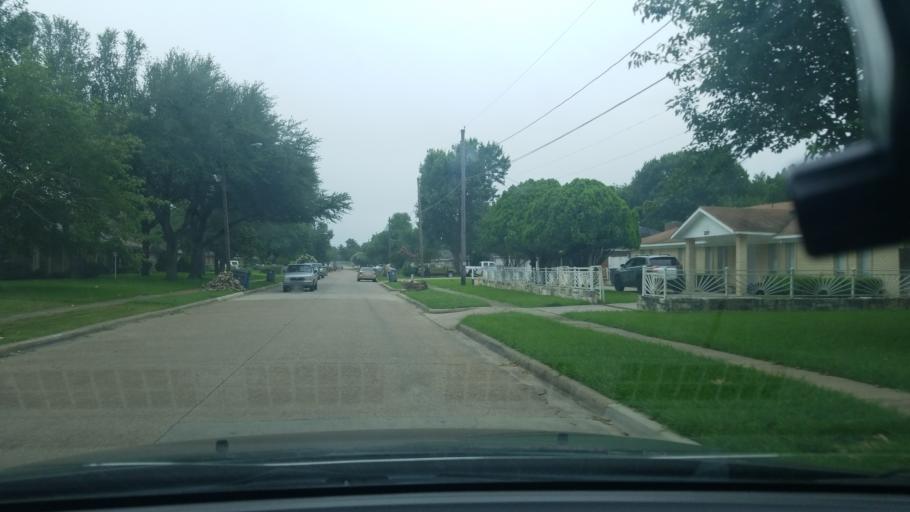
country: US
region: Texas
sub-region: Dallas County
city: Balch Springs
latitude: 32.7535
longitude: -96.6772
